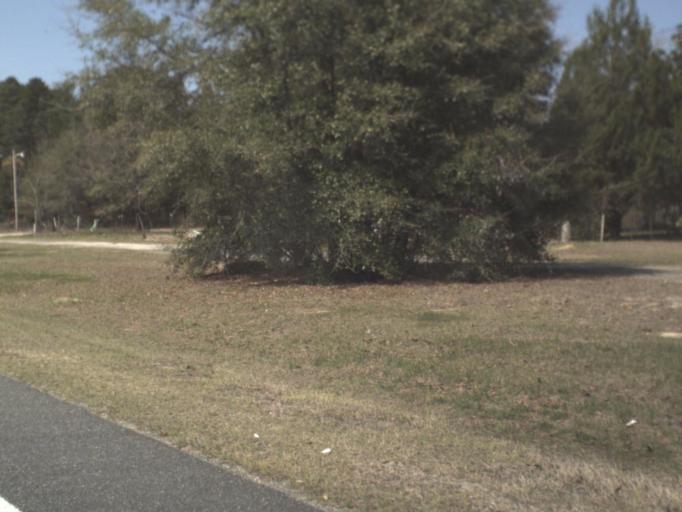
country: US
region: Florida
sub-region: Gadsden County
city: Gretna
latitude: 30.5251
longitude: -84.7999
